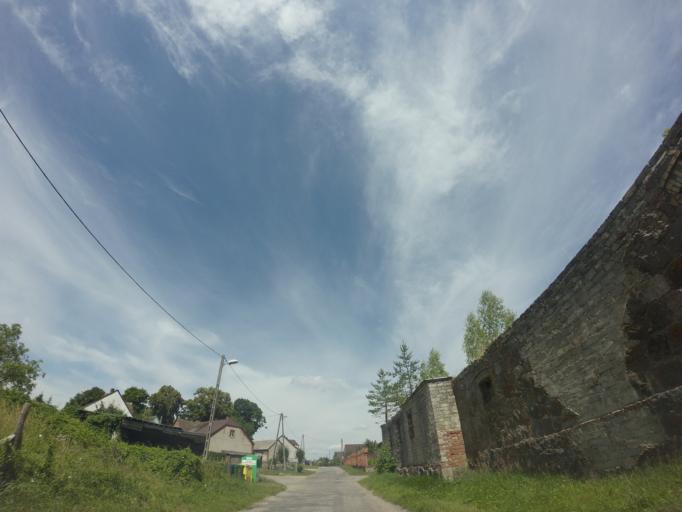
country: PL
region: West Pomeranian Voivodeship
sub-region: Powiat choszczenski
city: Recz
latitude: 53.3441
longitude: 15.5427
